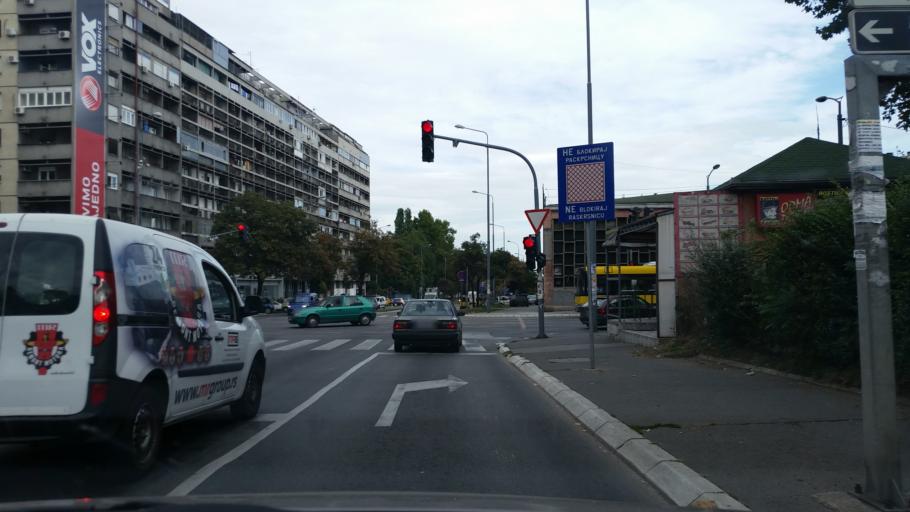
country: RS
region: Central Serbia
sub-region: Belgrade
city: Stari Grad
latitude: 44.8169
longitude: 20.4769
